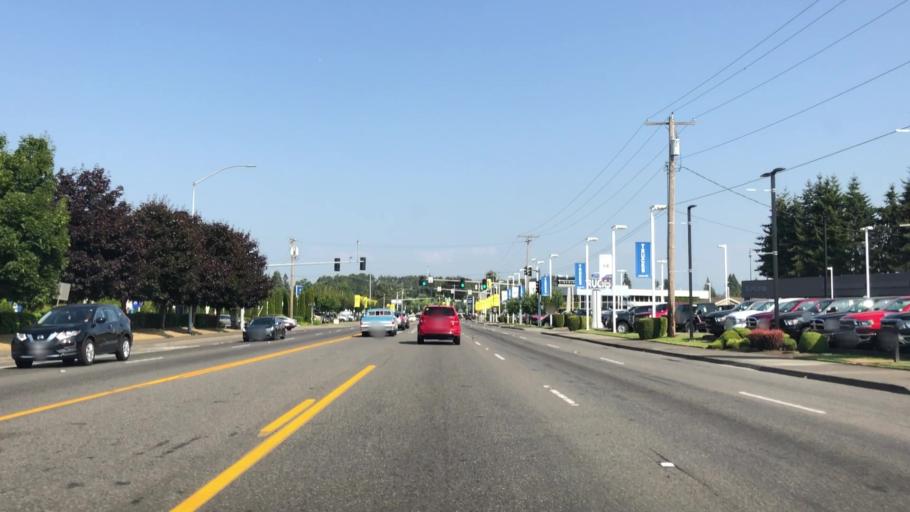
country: US
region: Washington
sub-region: Pierce County
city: Puyallup
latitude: 47.1996
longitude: -122.2972
